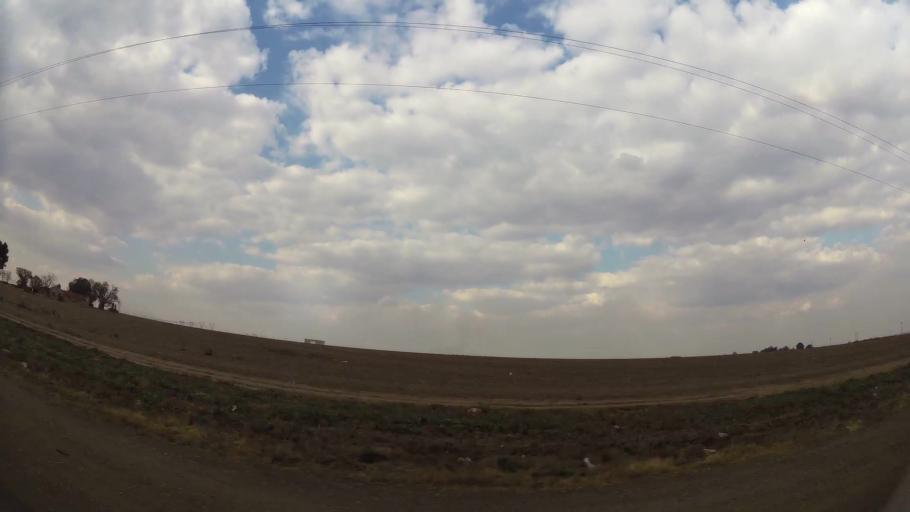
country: ZA
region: Mpumalanga
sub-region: Nkangala District Municipality
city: Delmas
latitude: -26.2573
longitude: 28.6340
